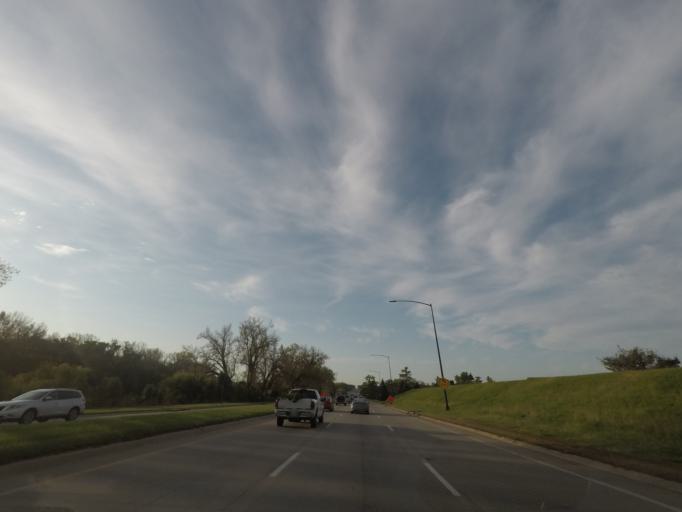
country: US
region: Iowa
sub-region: Polk County
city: Des Moines
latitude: 41.5777
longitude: -93.6450
